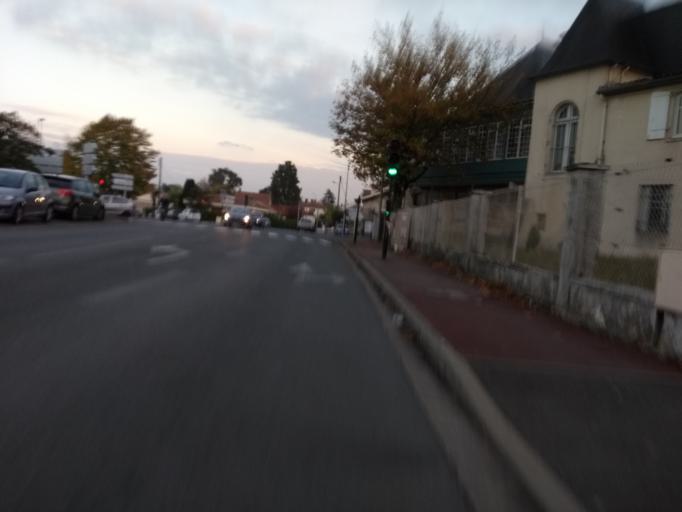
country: FR
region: Aquitaine
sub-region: Departement de la Gironde
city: Talence
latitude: 44.8069
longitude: -0.5867
